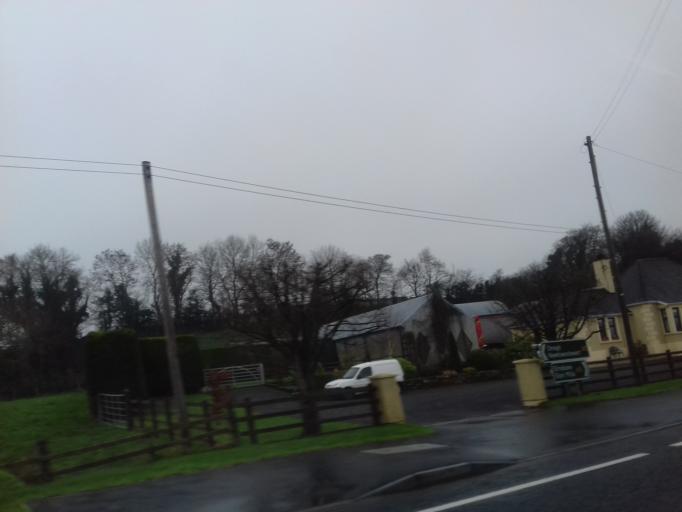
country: GB
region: Northern Ireland
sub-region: Strabane District
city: Sion Mills
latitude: 54.7635
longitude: -7.4633
